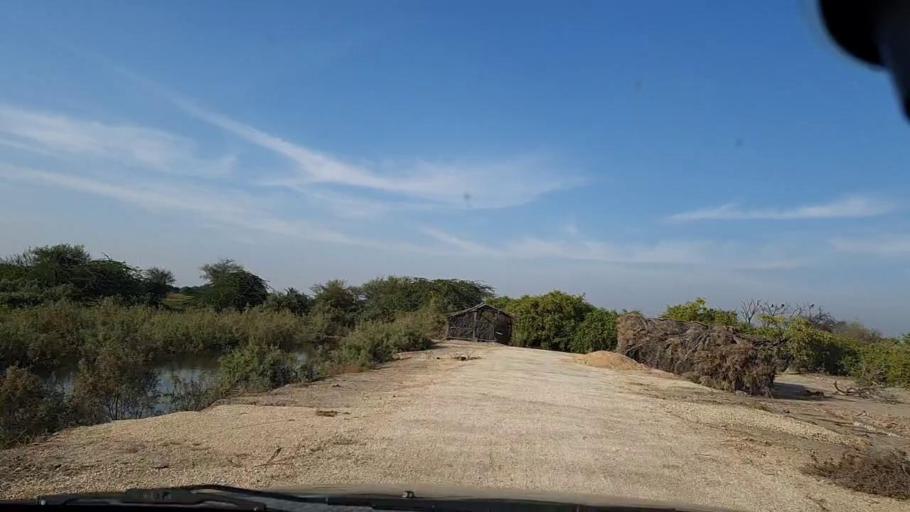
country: PK
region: Sindh
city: Mirpur Batoro
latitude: 24.6369
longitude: 68.2978
